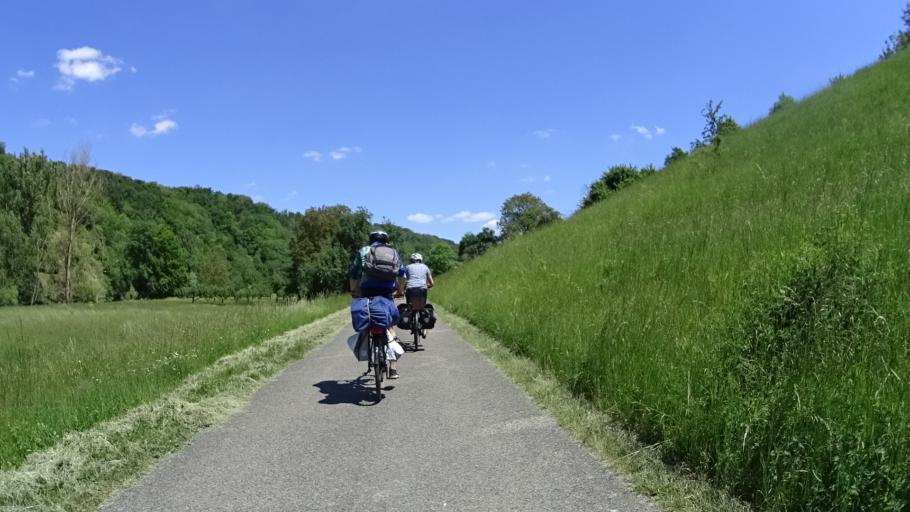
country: DE
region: Bavaria
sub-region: Regierungsbezirk Mittelfranken
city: Adelshofen
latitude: 49.4452
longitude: 10.1080
